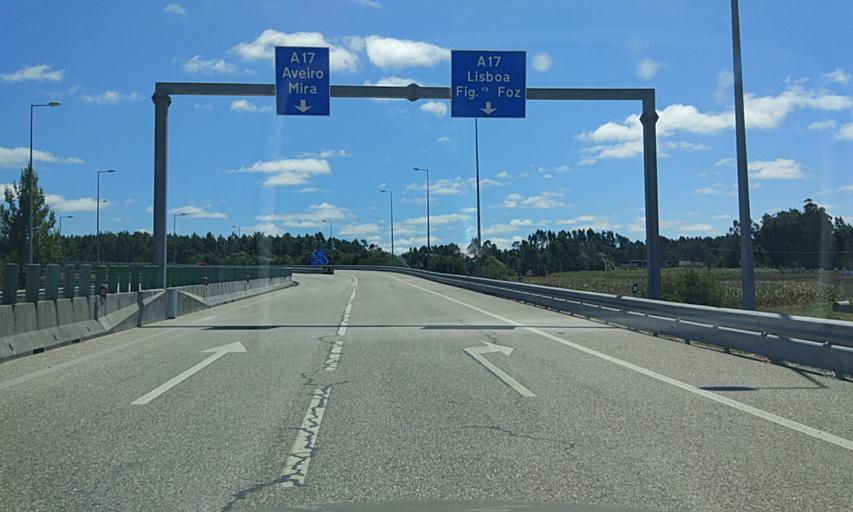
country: PT
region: Coimbra
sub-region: Montemor-O-Velho
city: Arazede
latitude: 40.3280
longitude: -8.7250
